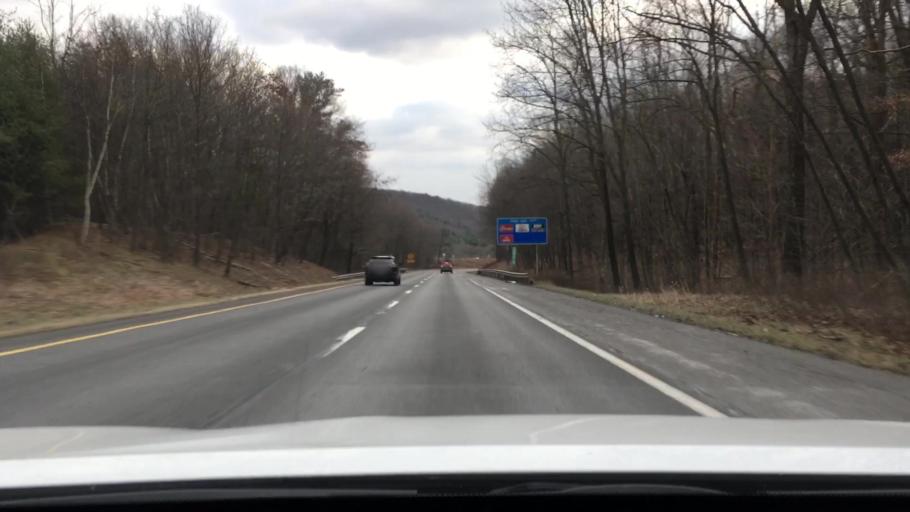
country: US
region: Pennsylvania
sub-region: Monroe County
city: Tannersville
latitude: 41.0560
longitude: -75.3219
